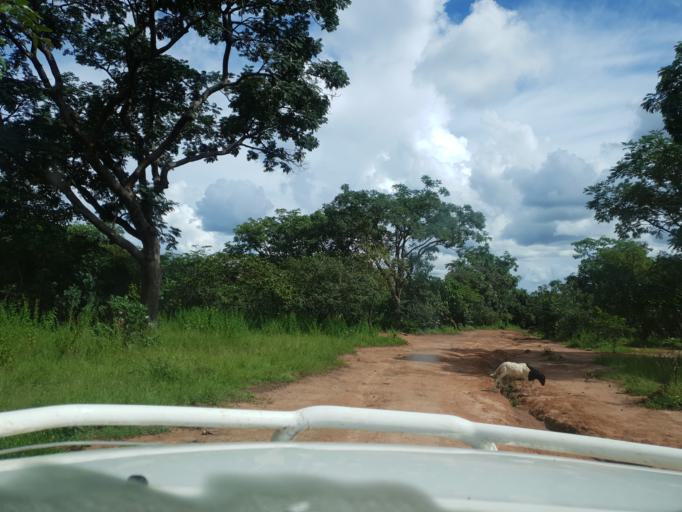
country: CI
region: Savanes
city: Tengrela
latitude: 10.4571
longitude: -6.7946
